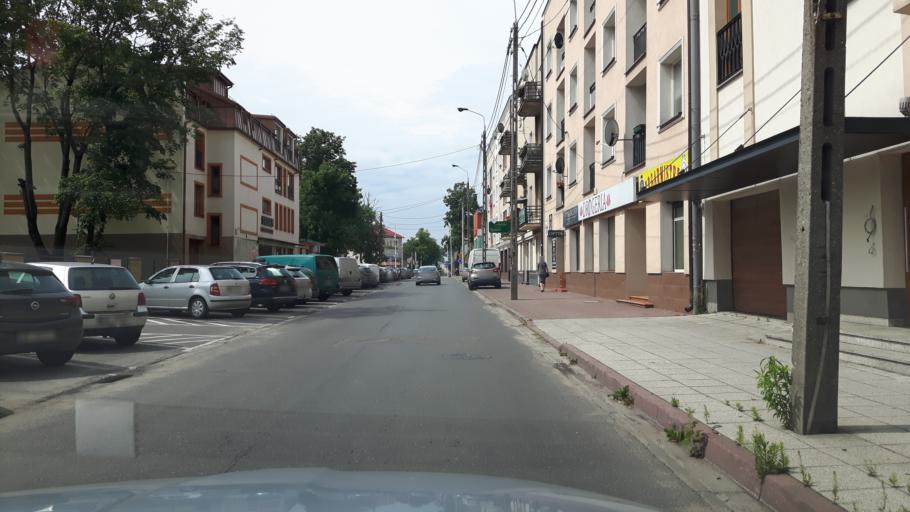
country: PL
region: Masovian Voivodeship
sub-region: Powiat wolominski
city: Wolomin
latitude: 52.3458
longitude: 21.2407
